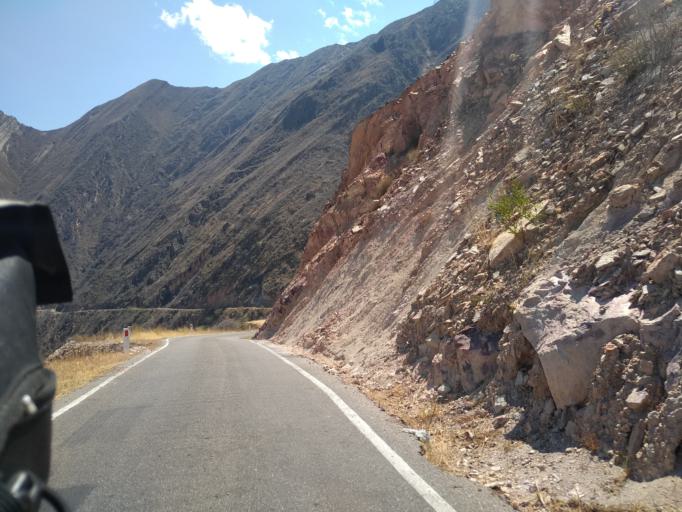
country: PE
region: Amazonas
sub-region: Provincia de Chachapoyas
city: Balsas
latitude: -6.8480
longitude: -77.9853
